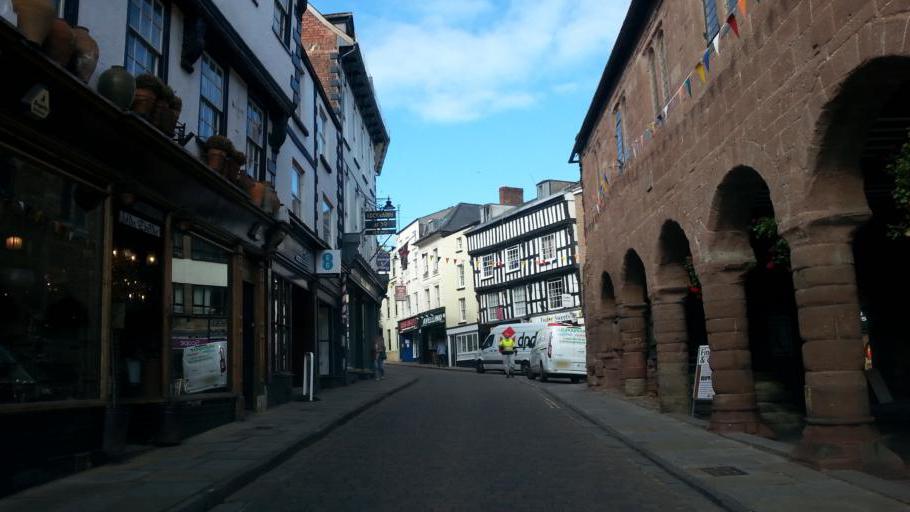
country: GB
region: England
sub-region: Herefordshire
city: Ross on Wye
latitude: 51.9141
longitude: -2.5840
